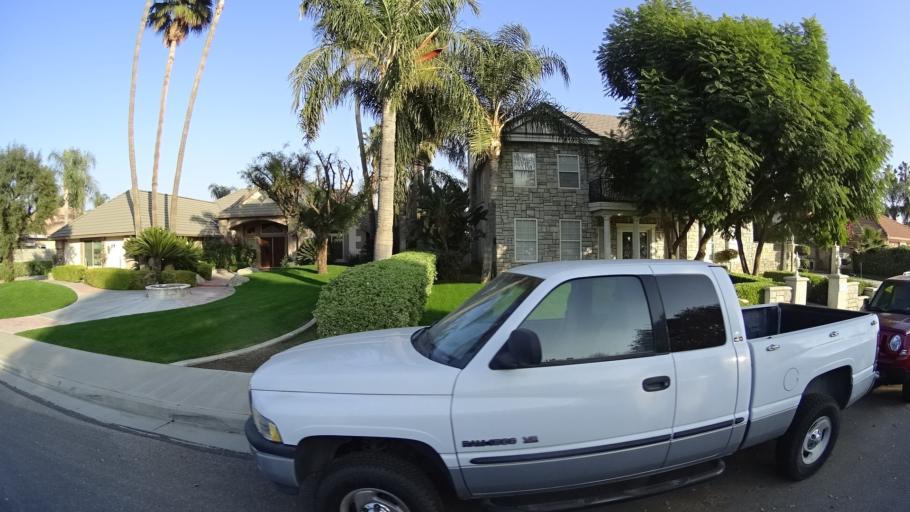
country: US
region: California
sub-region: Kern County
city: Rosedale
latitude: 35.3771
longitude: -119.1463
